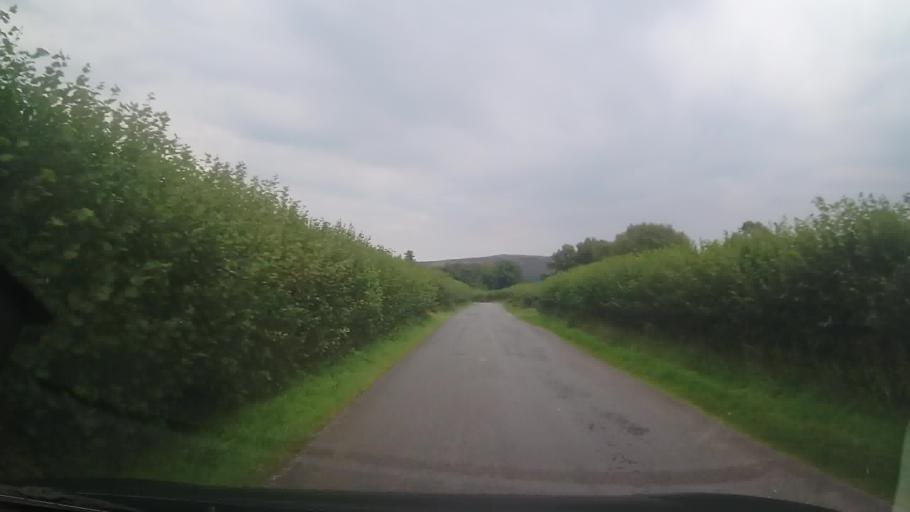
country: GB
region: Wales
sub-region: Sir Powys
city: Rhayader
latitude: 52.3054
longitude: -3.5318
